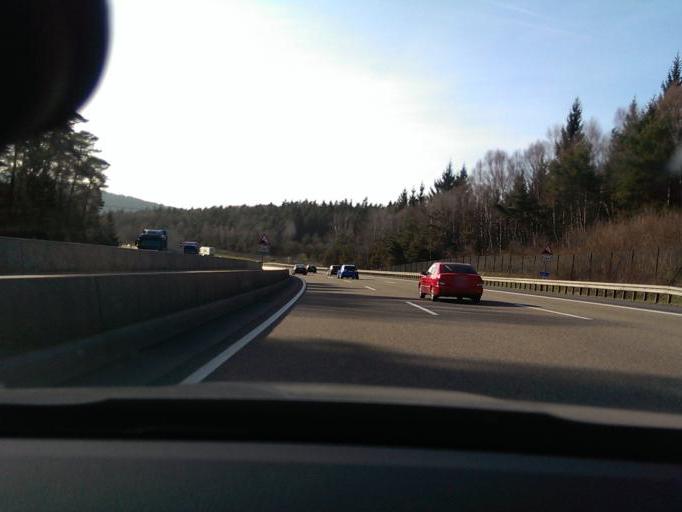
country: DE
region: Hesse
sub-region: Regierungsbezirk Kassel
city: Kirchheim
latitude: 50.8856
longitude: 9.5957
